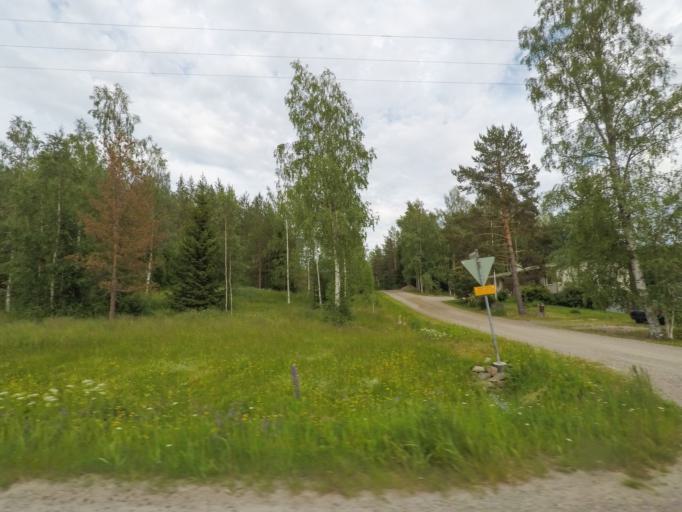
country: FI
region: Paijanne Tavastia
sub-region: Lahti
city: Hollola
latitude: 60.8787
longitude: 25.5049
